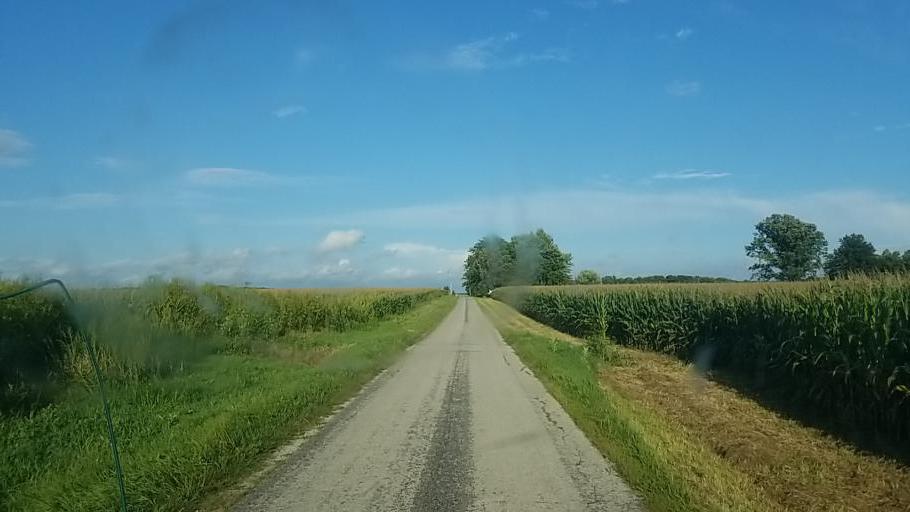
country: US
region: Ohio
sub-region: Crawford County
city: Bucyrus
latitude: 40.7395
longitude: -82.9655
